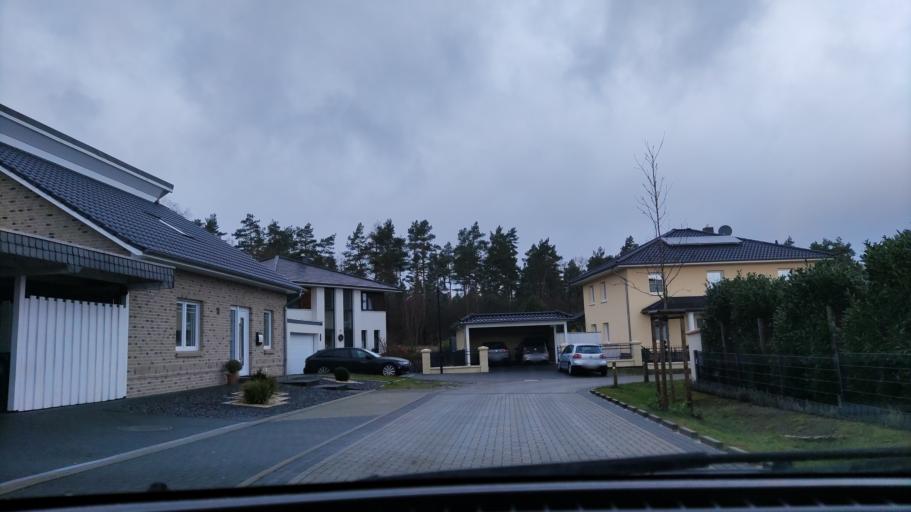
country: DE
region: Lower Saxony
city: Bienenbuttel
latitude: 53.1543
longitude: 10.4481
